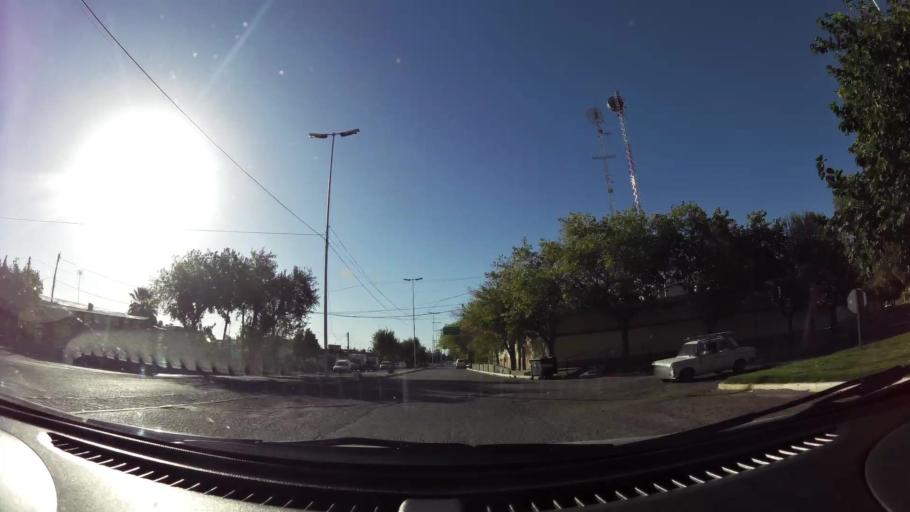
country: AR
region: San Juan
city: Villa Krause
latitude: -31.5585
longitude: -68.5147
